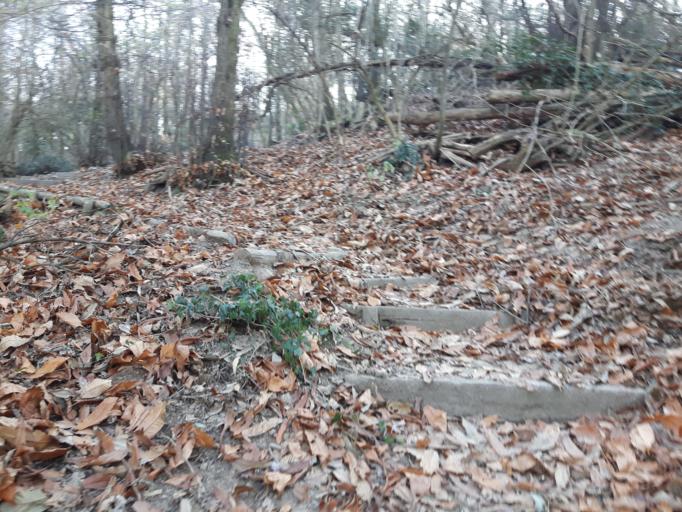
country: IT
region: Veneto
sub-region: Provincia di Padova
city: San Biagio
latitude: 45.3701
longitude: 11.7515
